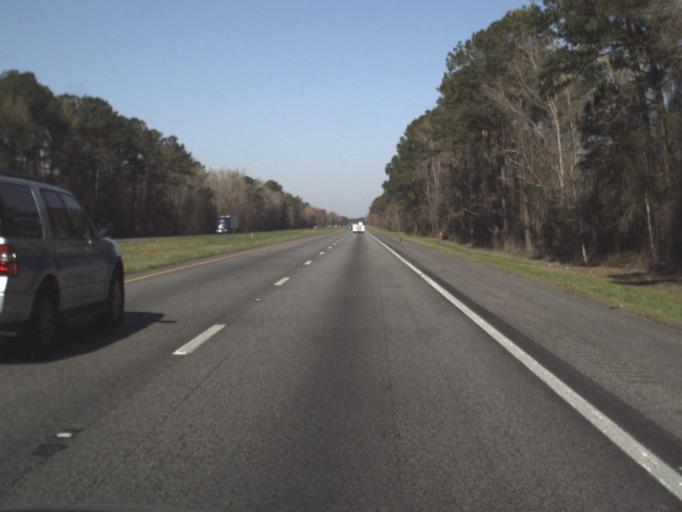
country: US
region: Florida
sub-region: Jefferson County
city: Monticello
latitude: 30.4626
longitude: -83.7870
